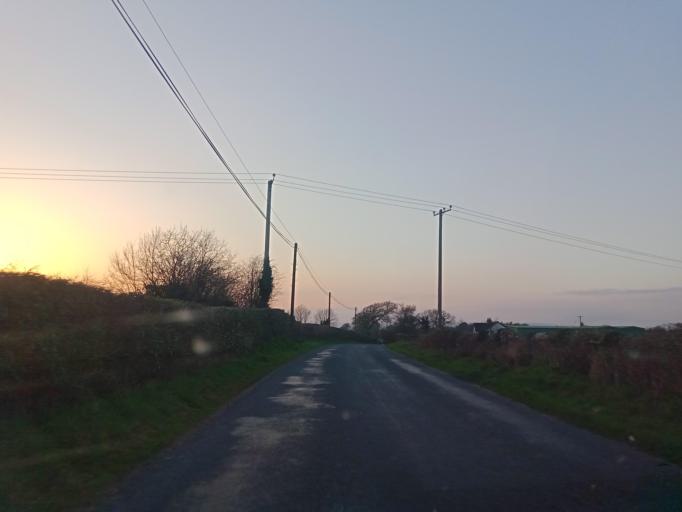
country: IE
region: Leinster
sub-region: Laois
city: Abbeyleix
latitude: 52.9502
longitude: -7.3525
